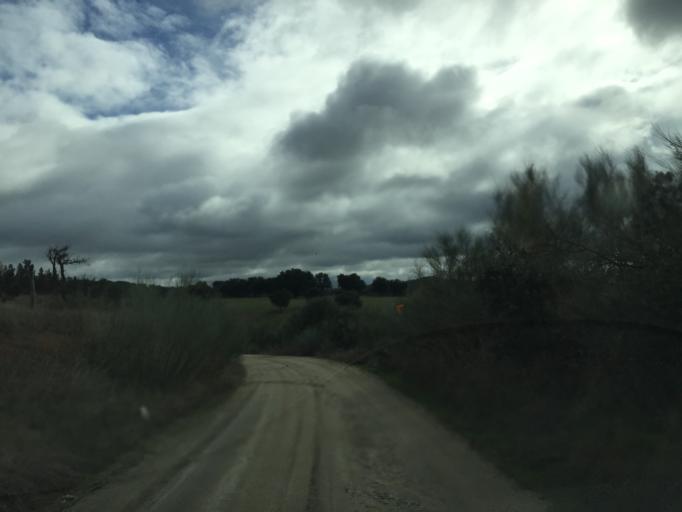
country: PT
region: Portalegre
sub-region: Alter do Chao
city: Alter do Chao
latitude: 39.2363
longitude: -7.6923
